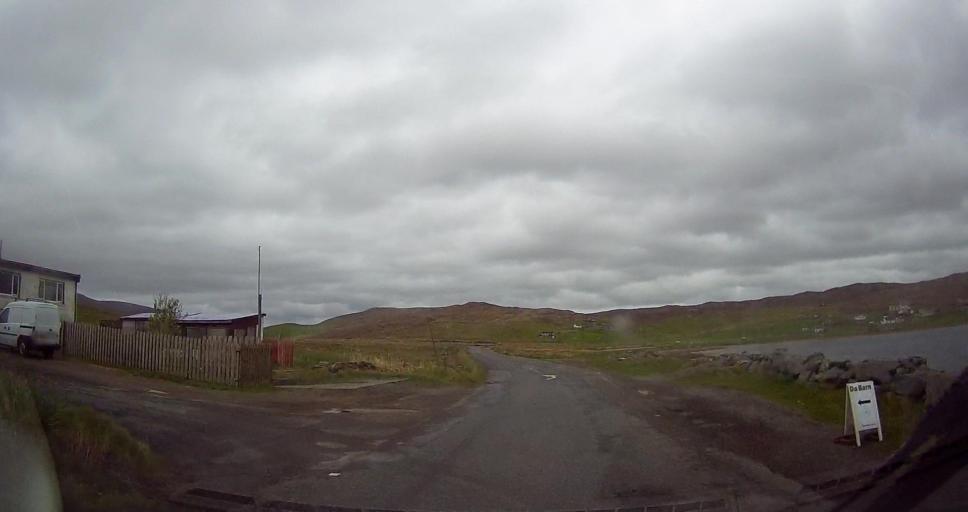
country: GB
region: Scotland
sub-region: Shetland Islands
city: Lerwick
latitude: 60.4900
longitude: -1.4631
